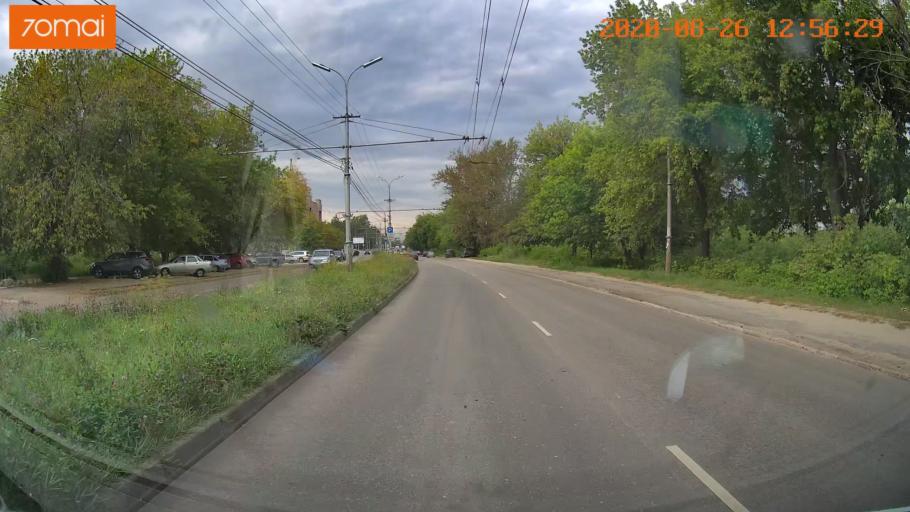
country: RU
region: Rjazan
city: Ryazan'
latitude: 54.6138
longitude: 39.7491
